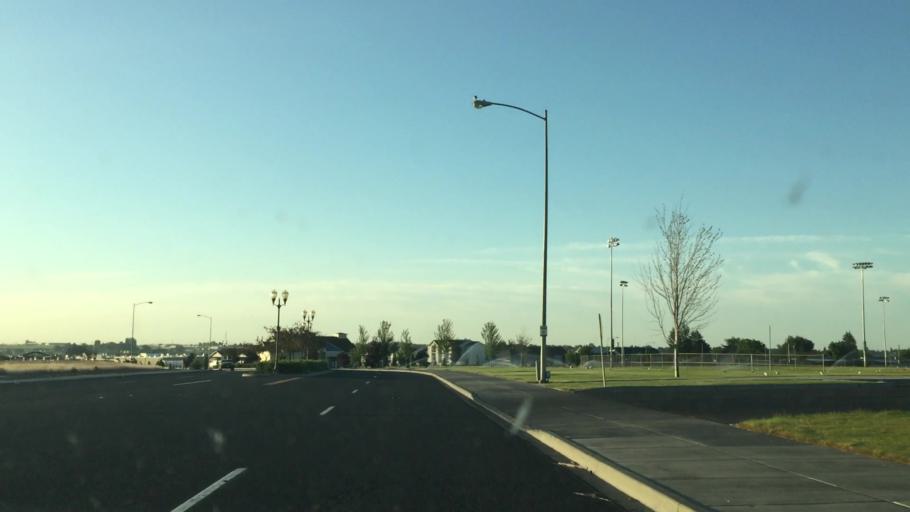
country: US
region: Washington
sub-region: Grant County
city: Moses Lake
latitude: 47.1442
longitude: -119.2892
